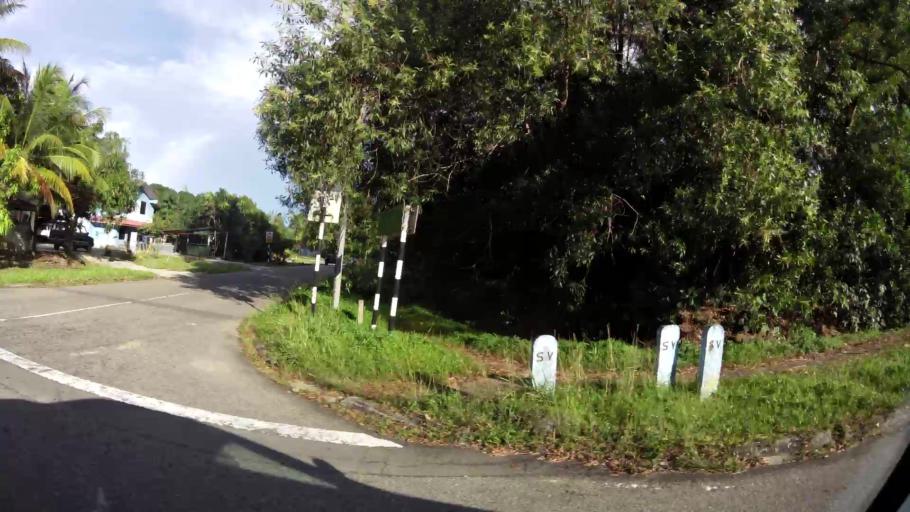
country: BN
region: Brunei and Muara
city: Bandar Seri Begawan
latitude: 4.9850
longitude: 114.9732
